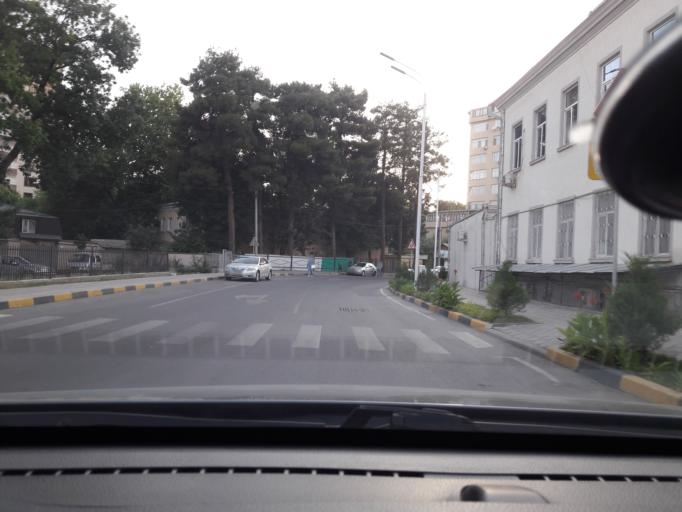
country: TJ
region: Dushanbe
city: Dushanbe
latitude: 38.5722
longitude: 68.7937
